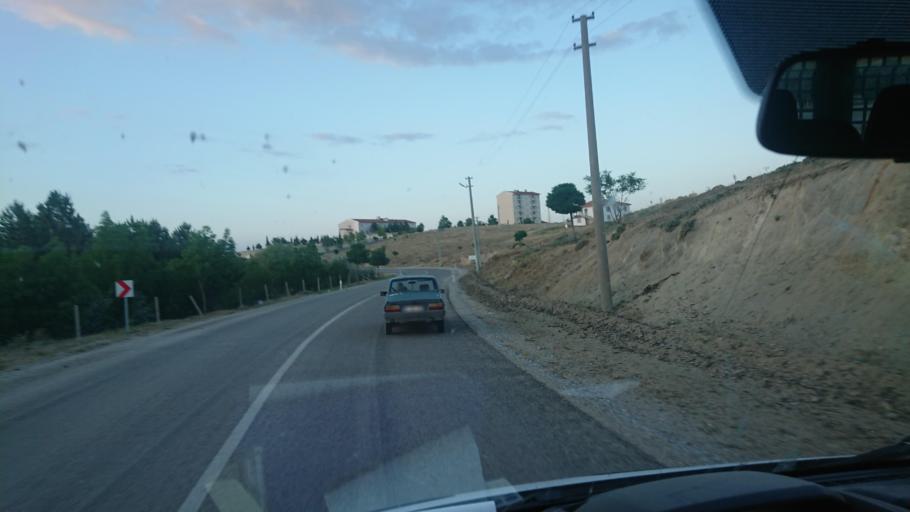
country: TR
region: Aksaray
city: Sariyahsi
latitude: 38.9709
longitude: 33.8293
